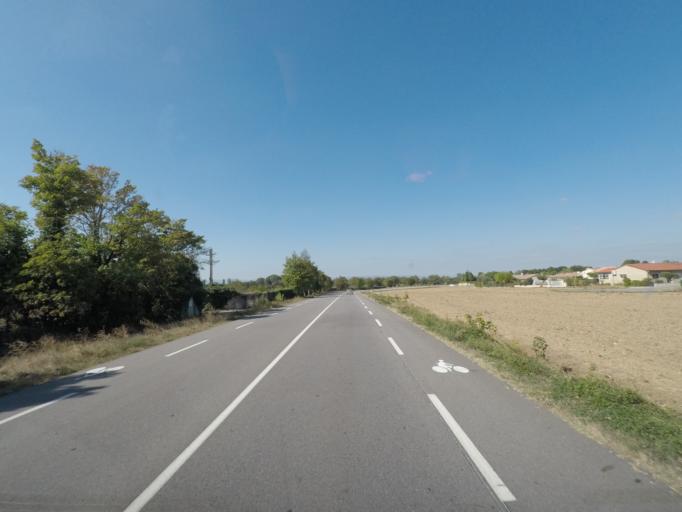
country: FR
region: Rhone-Alpes
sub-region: Departement de la Drome
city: Chabeuil
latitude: 44.8941
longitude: 5.0138
